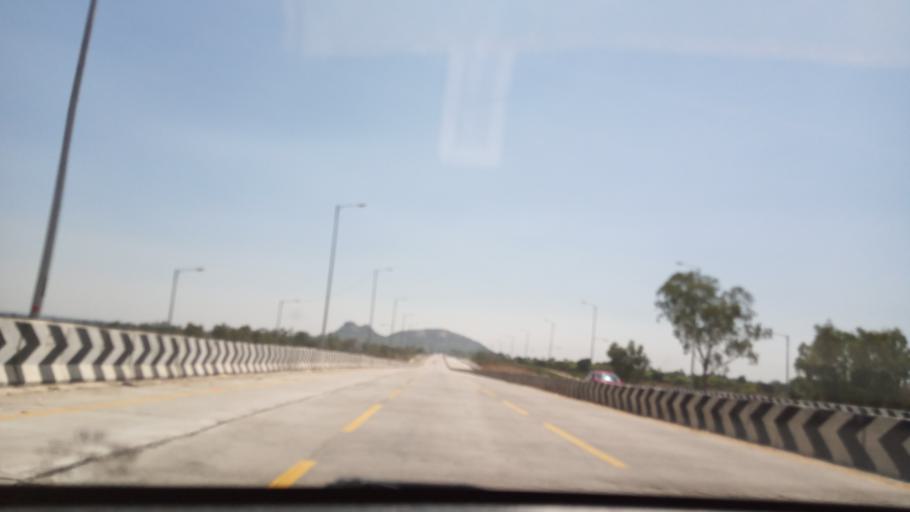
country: IN
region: Andhra Pradesh
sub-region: Chittoor
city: Palmaner
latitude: 13.1855
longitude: 78.6048
